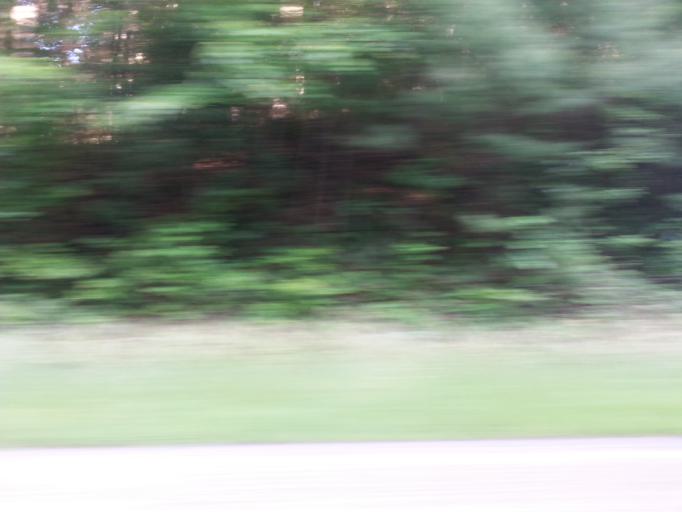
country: US
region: Georgia
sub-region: Union County
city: Blairsville
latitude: 34.8192
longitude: -83.8295
